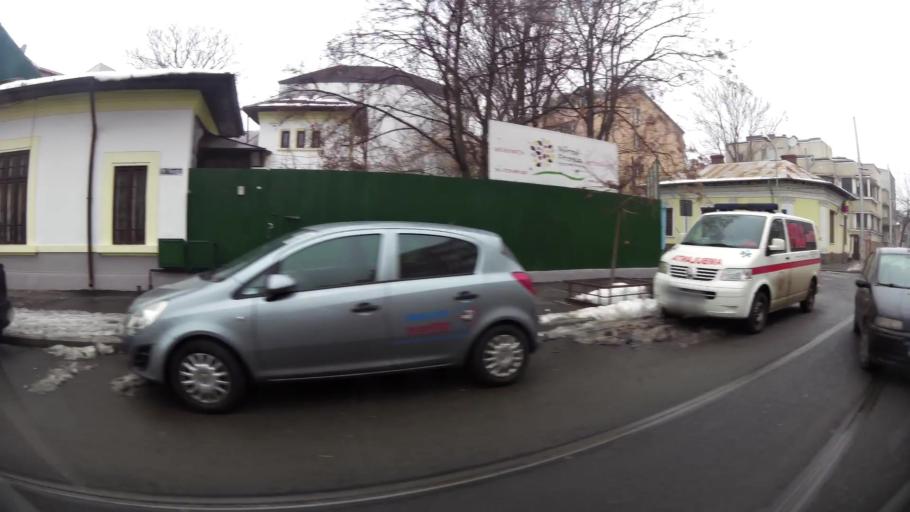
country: RO
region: Bucuresti
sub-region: Municipiul Bucuresti
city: Bucharest
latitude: 44.4501
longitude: 26.1064
